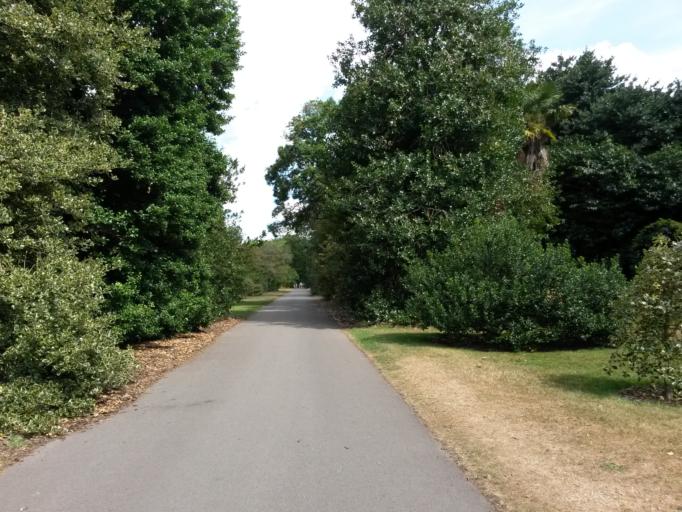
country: GB
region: England
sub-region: Greater London
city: Brentford
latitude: 51.4757
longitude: -0.2964
